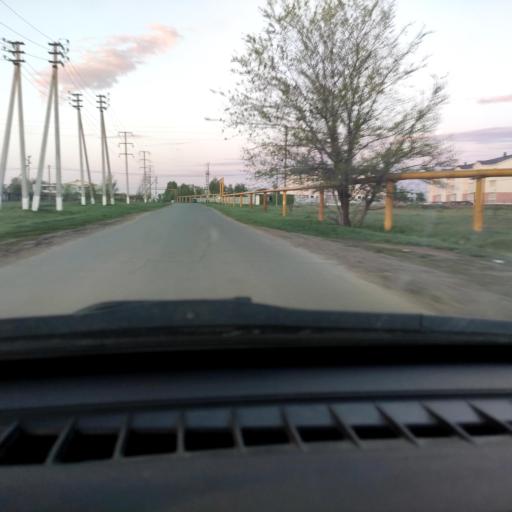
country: RU
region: Samara
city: Podstepki
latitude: 53.5217
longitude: 49.1134
